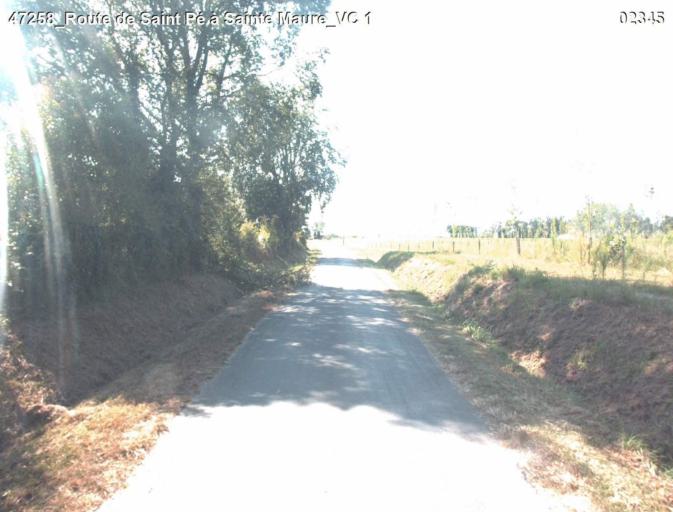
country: FR
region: Midi-Pyrenees
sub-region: Departement du Gers
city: Montreal
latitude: 44.0128
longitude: 0.1482
